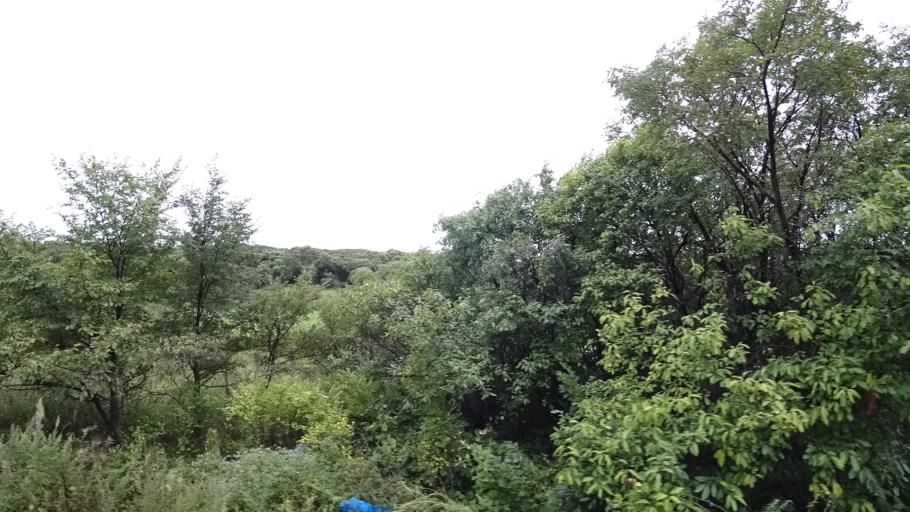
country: RU
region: Primorskiy
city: Monastyrishche
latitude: 44.2681
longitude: 132.4037
